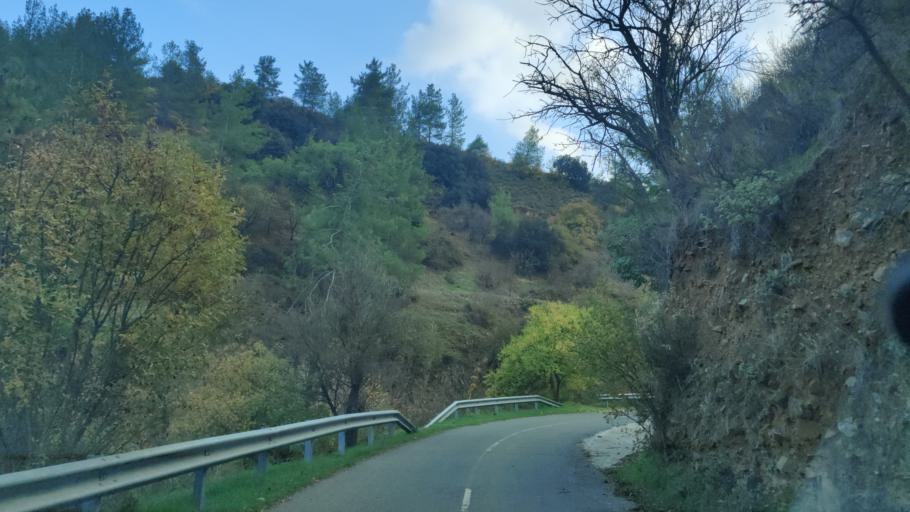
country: CY
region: Lefkosia
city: Lefka
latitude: 35.0602
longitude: 32.7354
